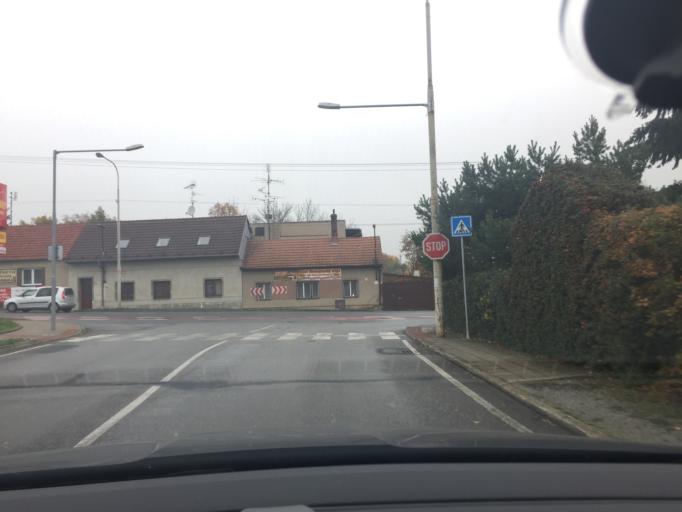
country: CZ
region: South Moravian
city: Rousinov
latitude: 49.2012
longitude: 16.8767
